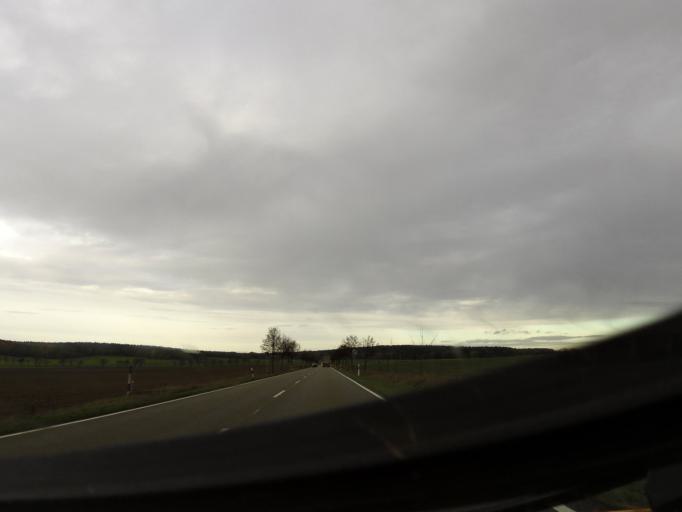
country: DE
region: Saxony-Anhalt
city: Kalbe
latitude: 52.6082
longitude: 11.3230
